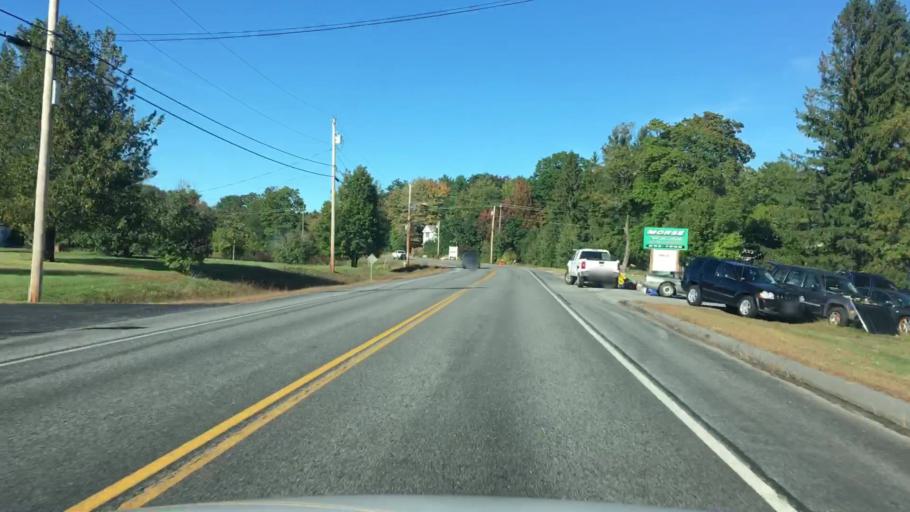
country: US
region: Maine
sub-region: Androscoggin County
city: Lisbon Falls
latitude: 44.0154
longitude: -70.0683
